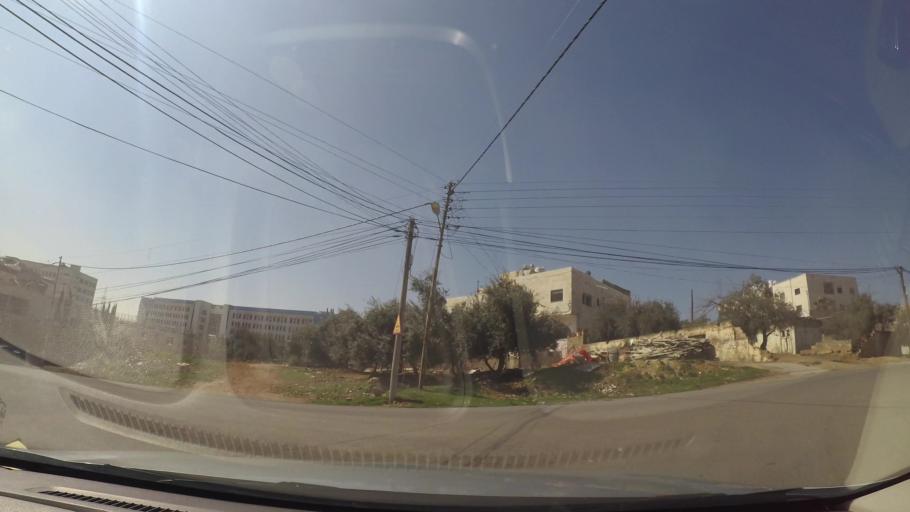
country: JO
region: Amman
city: Al Bunayyat ash Shamaliyah
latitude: 31.8920
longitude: 35.8953
